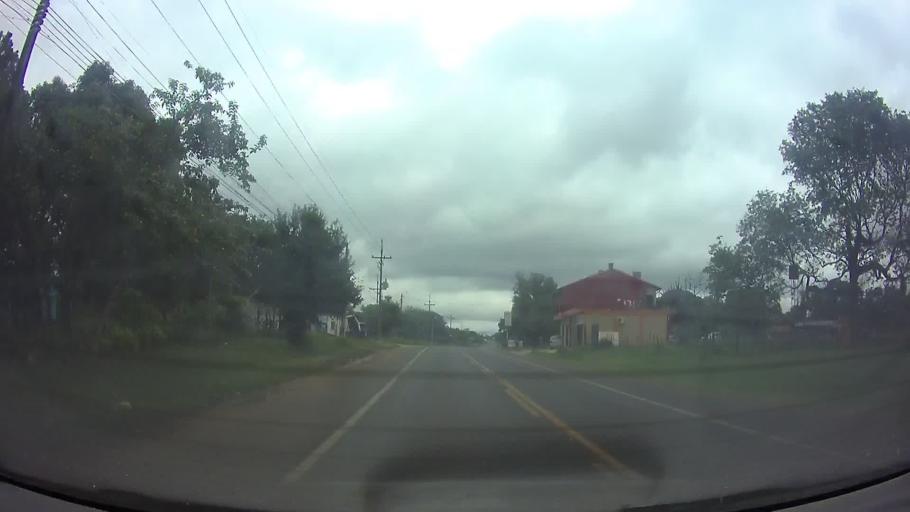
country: PY
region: Central
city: Guarambare
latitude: -25.5000
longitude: -57.4869
